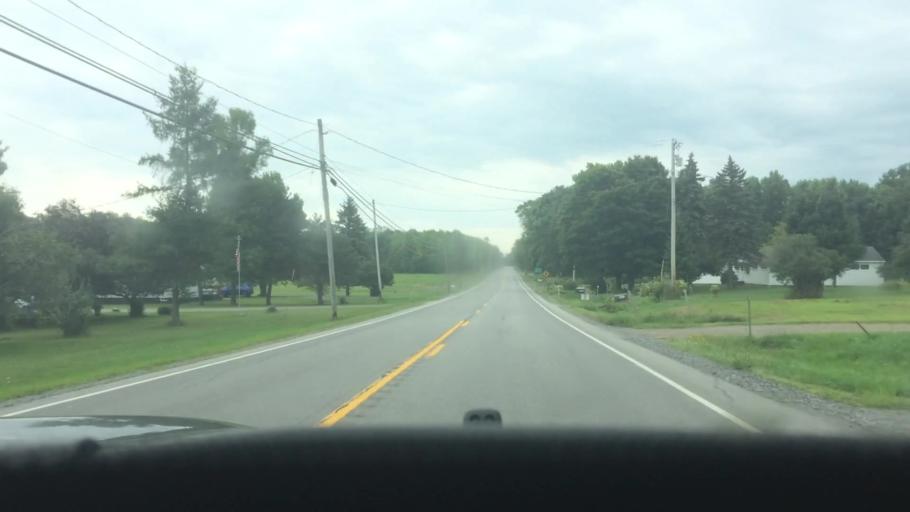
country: US
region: New York
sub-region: St. Lawrence County
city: Ogdensburg
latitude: 44.6552
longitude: -75.4477
